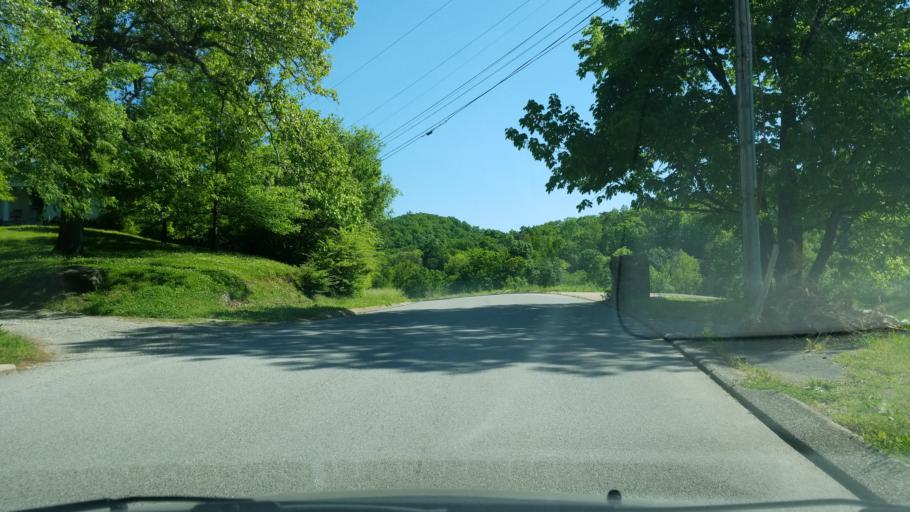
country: US
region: Tennessee
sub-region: Hamilton County
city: Walden
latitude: 35.1450
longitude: -85.3000
